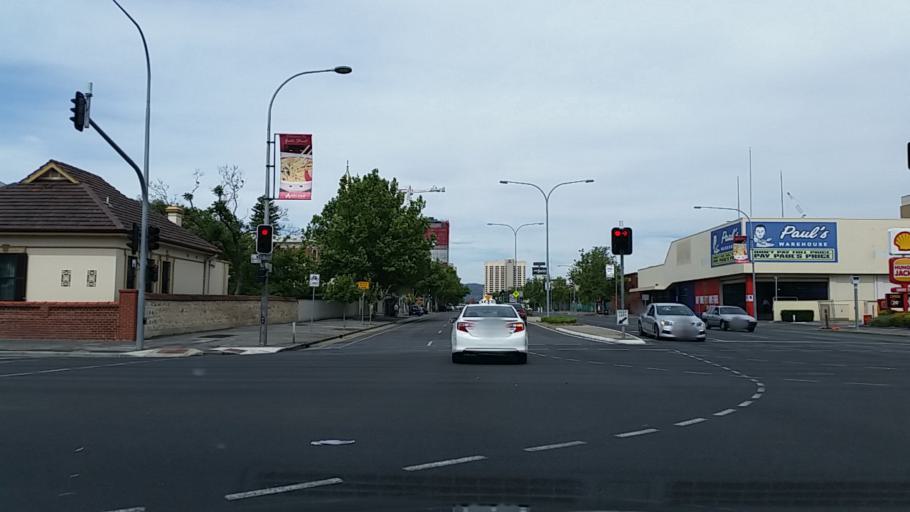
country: AU
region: South Australia
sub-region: Adelaide
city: Adelaide
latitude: -34.9292
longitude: 138.5877
